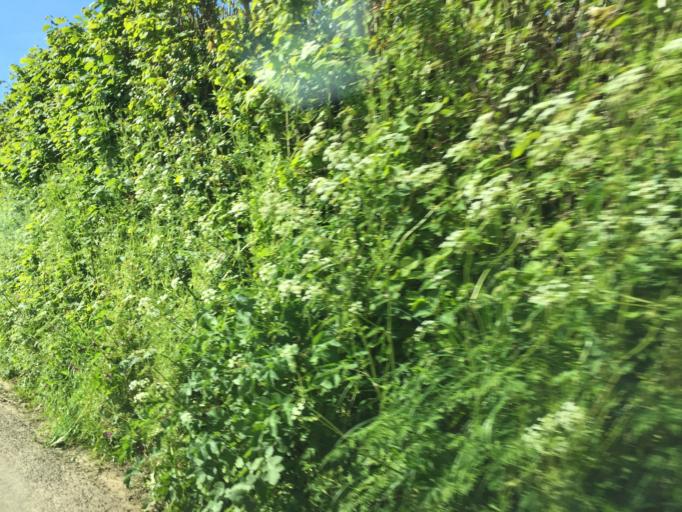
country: GB
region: England
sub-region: Wiltshire
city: Luckington
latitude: 51.5724
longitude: -2.2497
